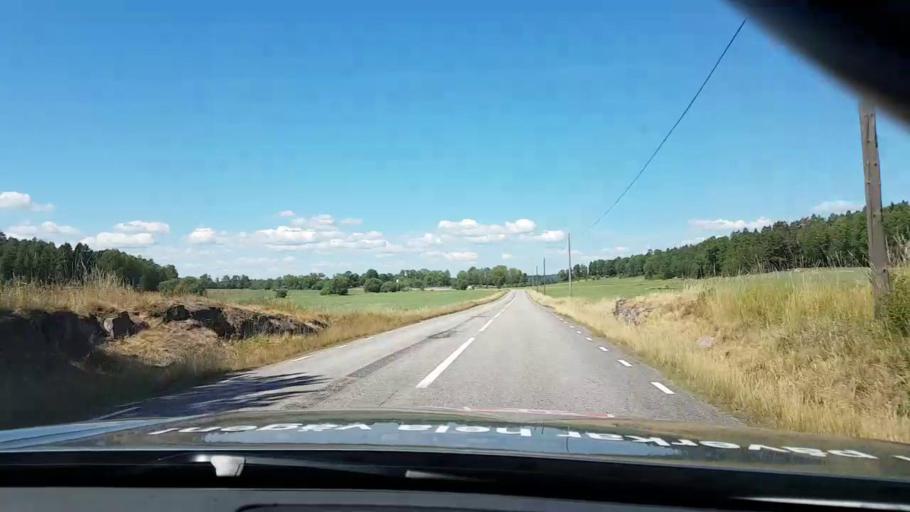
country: SE
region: Kalmar
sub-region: Vasterviks Kommun
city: Forserum
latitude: 57.9359
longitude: 16.5035
